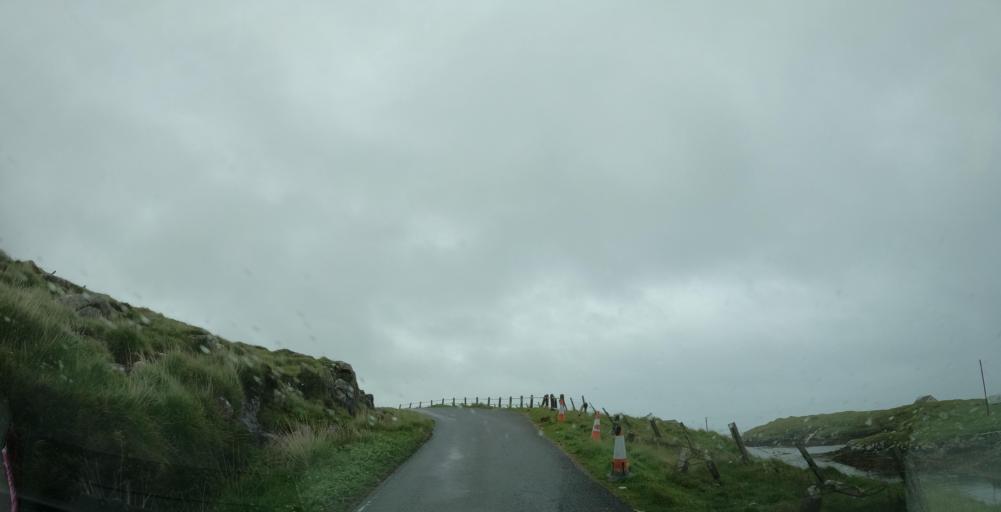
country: GB
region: Scotland
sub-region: Eilean Siar
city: Barra
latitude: 56.9760
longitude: -7.4222
